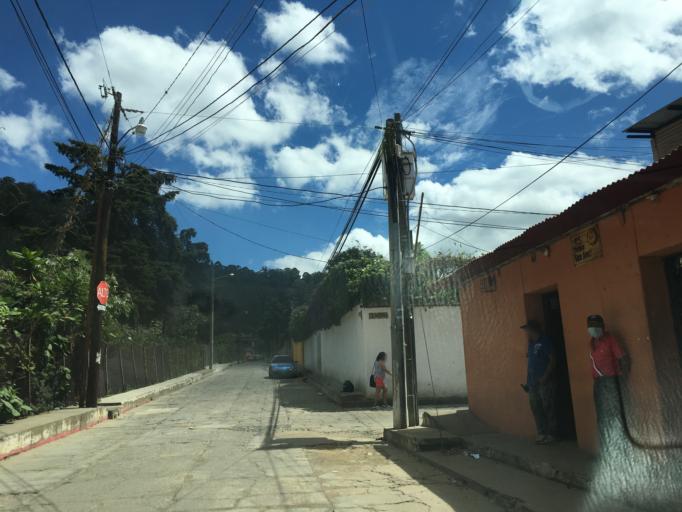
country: GT
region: Sacatepequez
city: Antigua Guatemala
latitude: 14.5638
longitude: -90.7266
